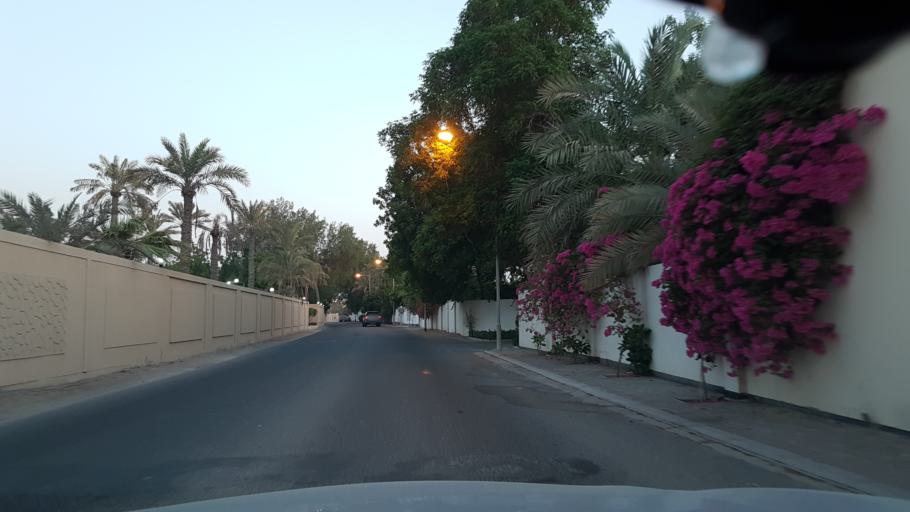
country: BH
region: Manama
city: Jidd Hafs
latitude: 26.2265
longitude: 50.4890
